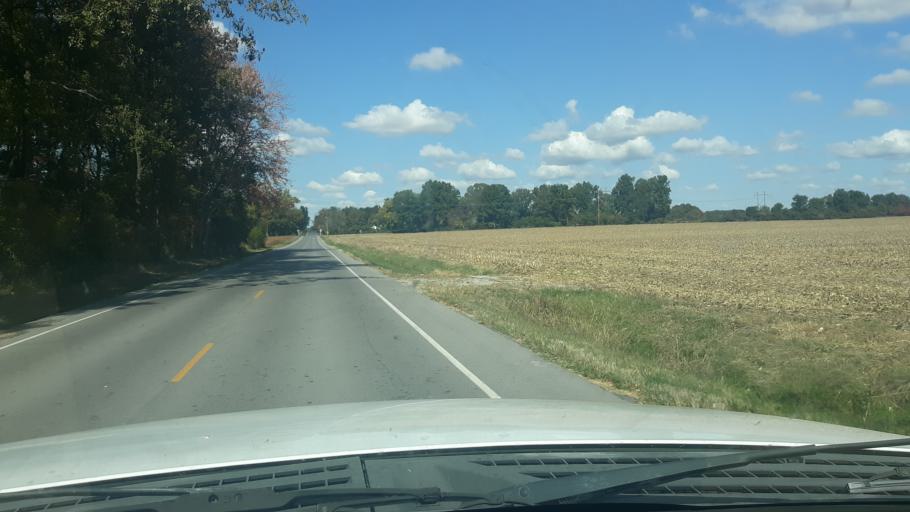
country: US
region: Illinois
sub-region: Saline County
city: Eldorado
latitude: 37.8083
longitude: -88.4848
